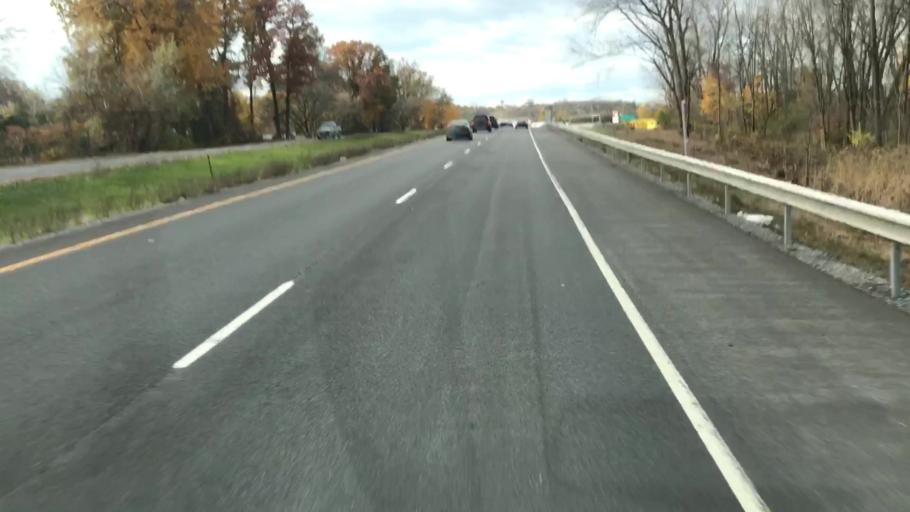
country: US
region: New York
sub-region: Onondaga County
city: Lakeland
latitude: 43.1173
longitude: -76.2555
